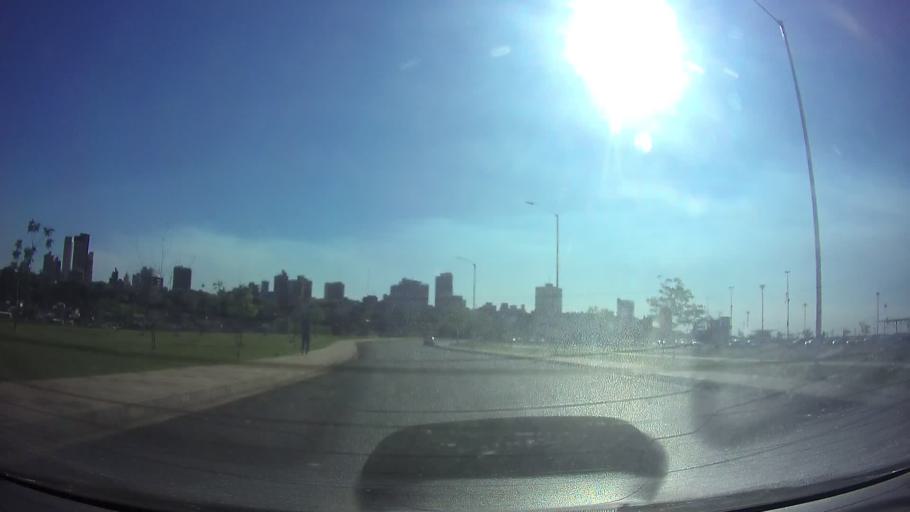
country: PY
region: Asuncion
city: Asuncion
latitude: -25.2776
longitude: -57.6297
